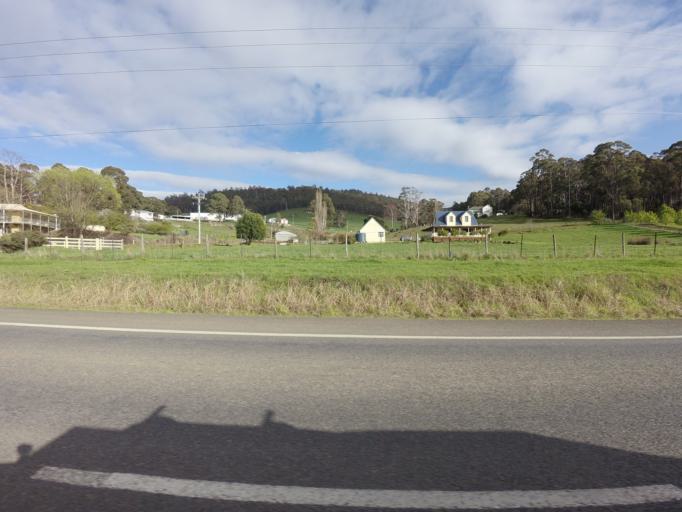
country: AU
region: Tasmania
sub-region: Huon Valley
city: Franklin
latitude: -43.0605
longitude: 147.0285
